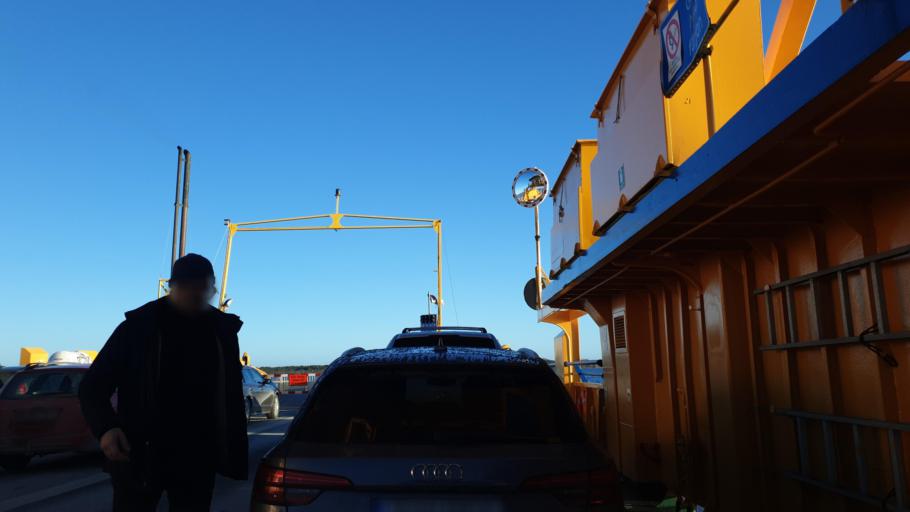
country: SE
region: Gotland
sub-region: Gotland
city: Slite
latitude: 57.8654
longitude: 19.0628
